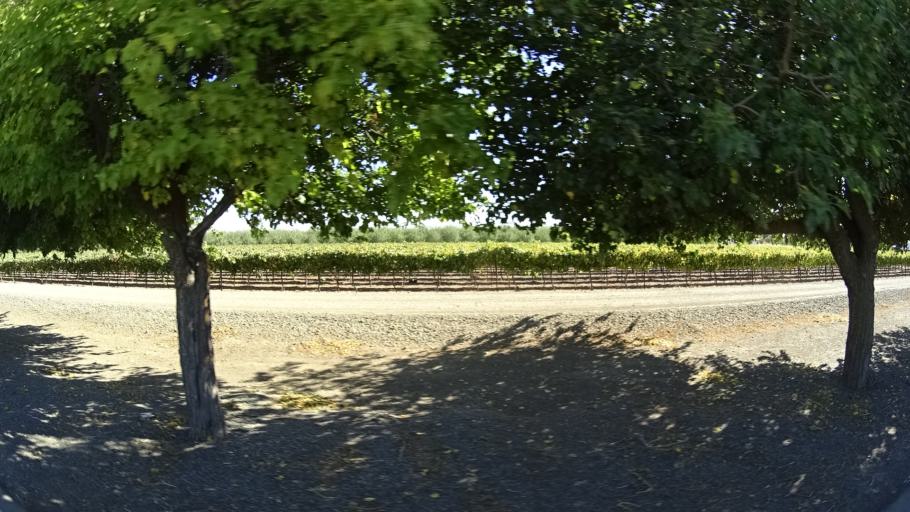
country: US
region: California
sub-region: Yolo County
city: Winters
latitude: 38.5333
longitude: -121.9711
